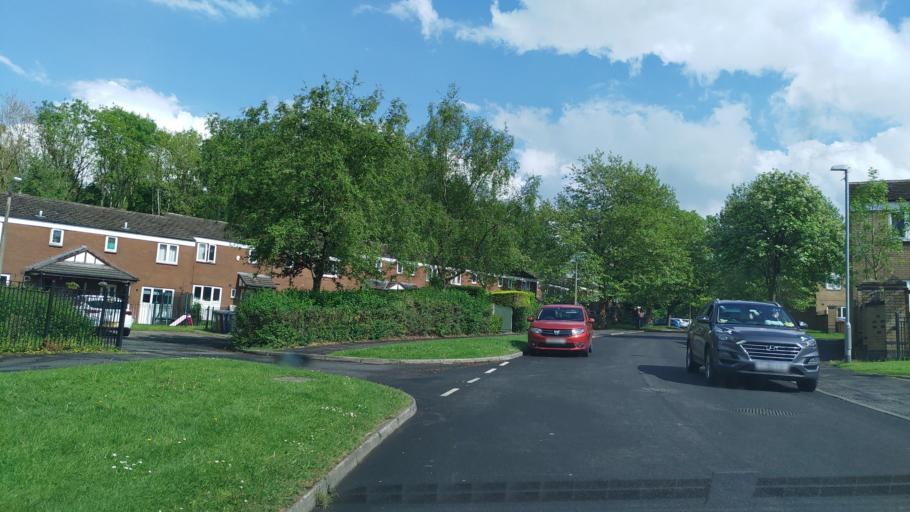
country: GB
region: England
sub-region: Lancashire
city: Clayton-le-Woods
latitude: 53.7157
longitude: -2.6363
